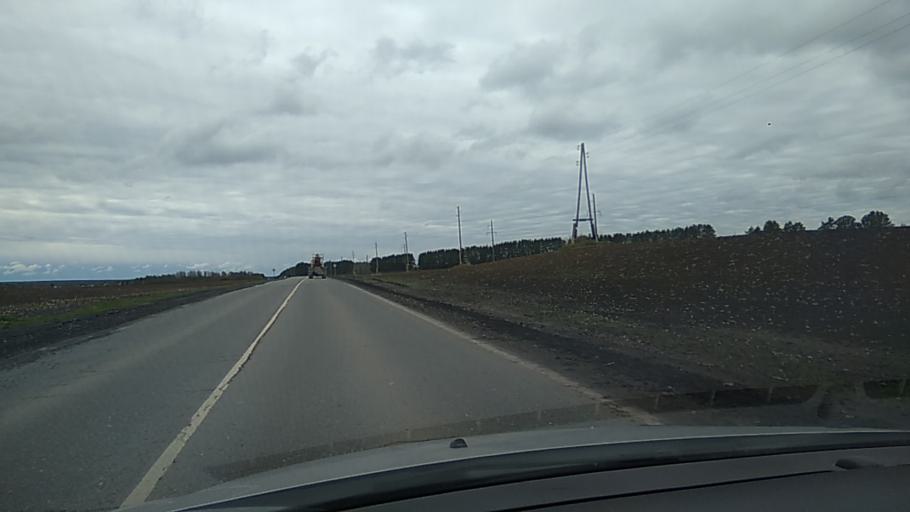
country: RU
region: Tjumen
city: Chervishevo
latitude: 56.8974
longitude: 65.4003
